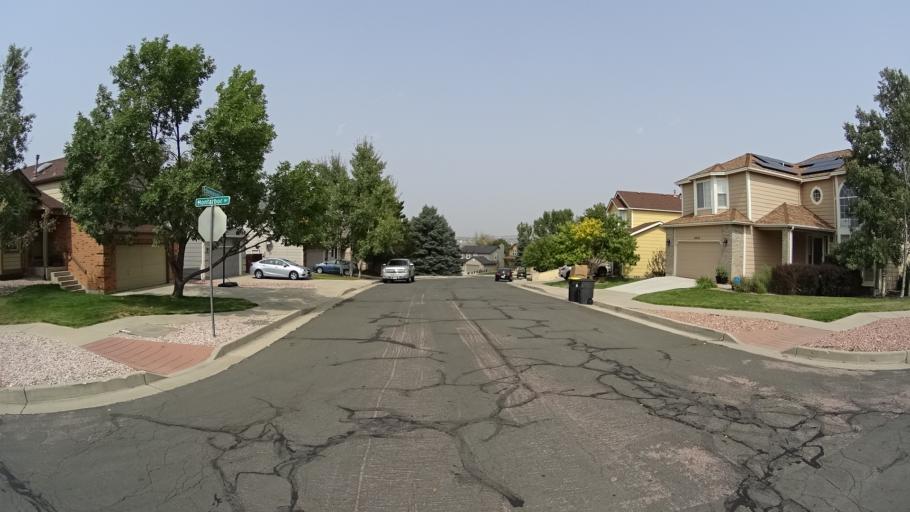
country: US
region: Colorado
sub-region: El Paso County
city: Cimarron Hills
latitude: 38.9194
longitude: -104.7497
